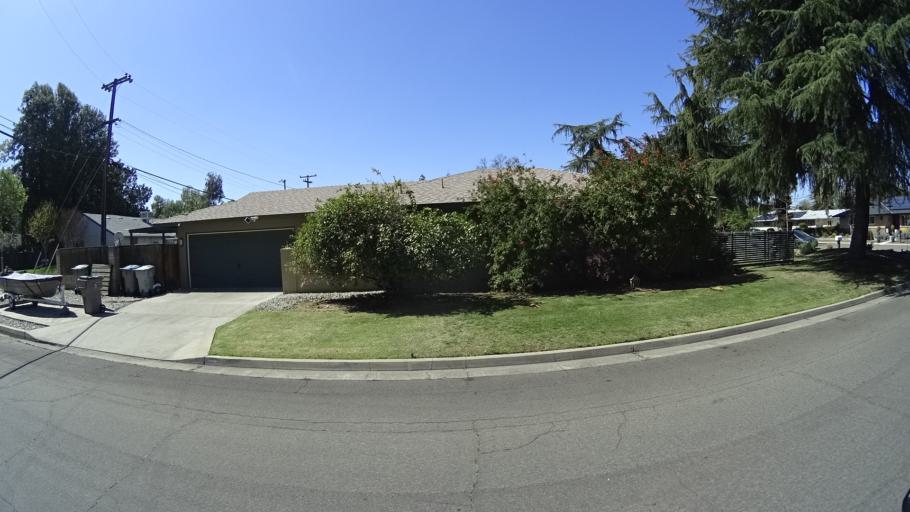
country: US
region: California
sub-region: Fresno County
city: Fresno
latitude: 36.8103
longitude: -119.8219
